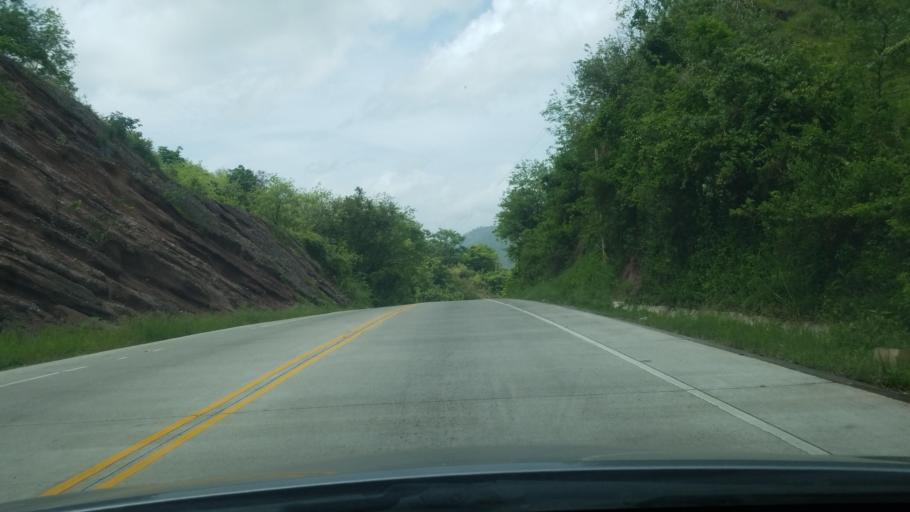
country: HN
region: Copan
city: Veracruz
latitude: 14.9146
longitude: -88.7537
